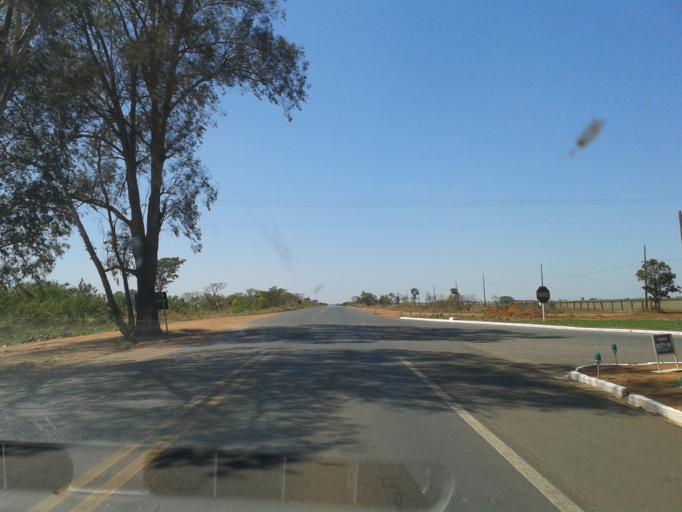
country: BR
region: Minas Gerais
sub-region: Uberaba
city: Uberaba
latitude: -19.3152
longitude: -47.5710
